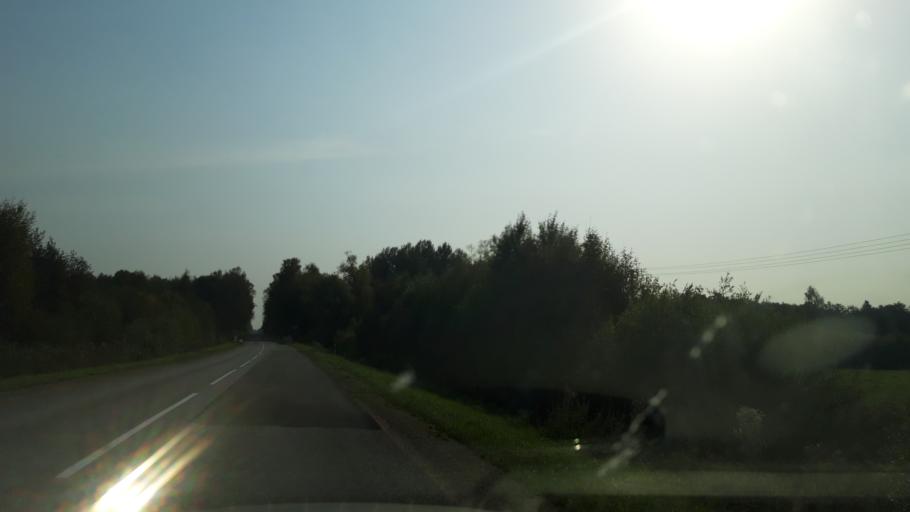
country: LV
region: Burtnieki
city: Matisi
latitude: 57.6559
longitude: 25.2300
